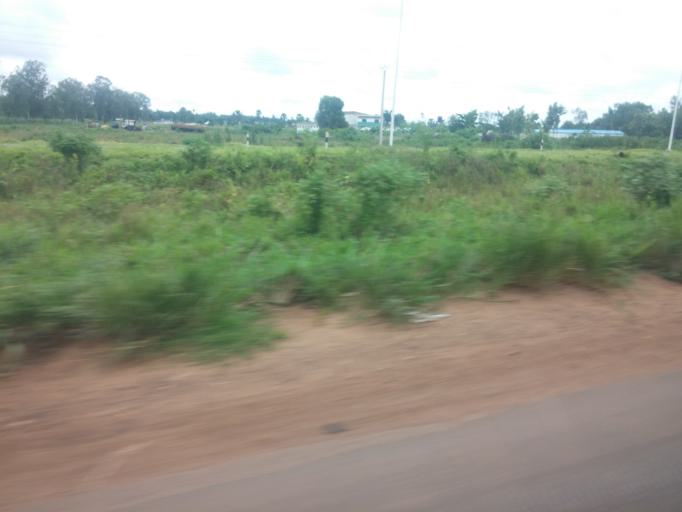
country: TG
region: Maritime
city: Tsevie
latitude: 6.3115
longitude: 1.2164
